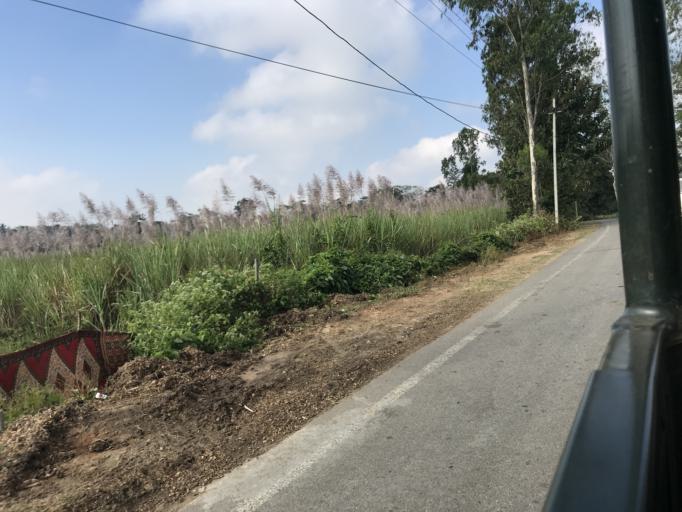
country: IN
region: Karnataka
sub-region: Mysore
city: Heggadadevankote
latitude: 11.9477
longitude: 76.2490
